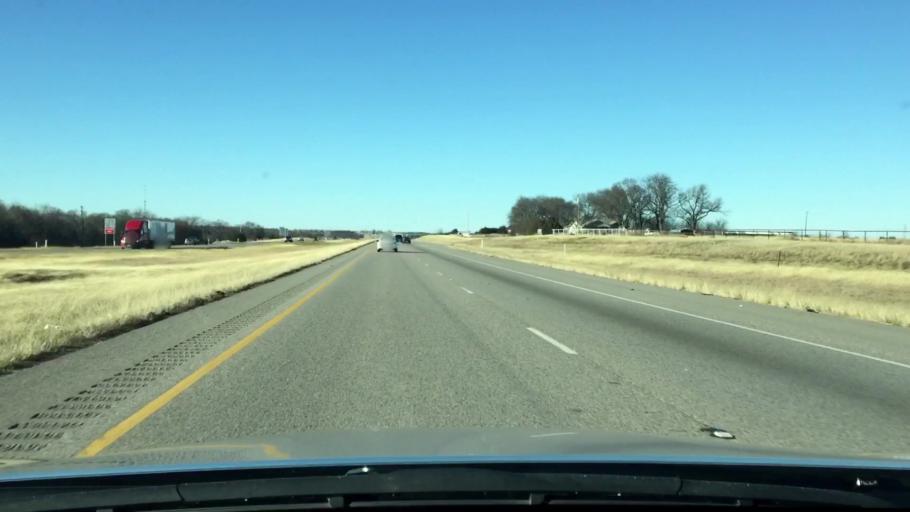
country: US
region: Texas
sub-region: Johnson County
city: Grandview
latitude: 32.2323
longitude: -97.1547
